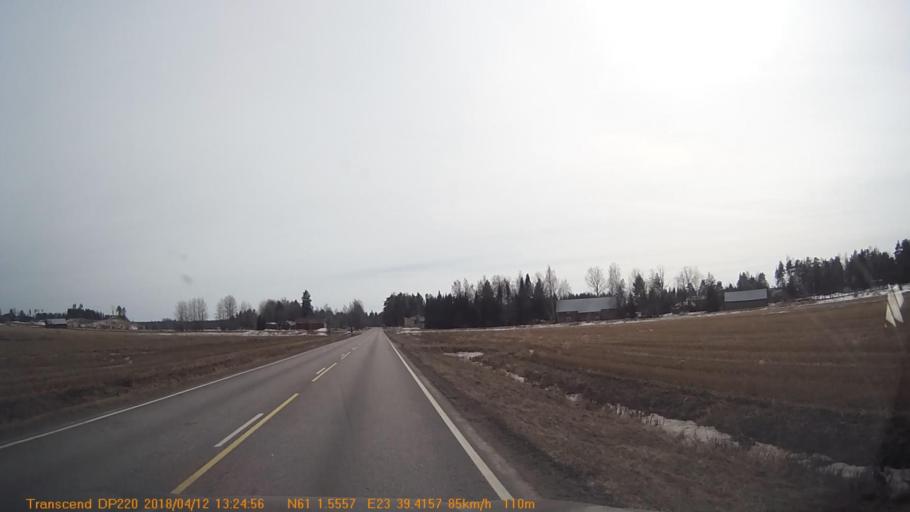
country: FI
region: Pirkanmaa
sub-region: Etelae-Pirkanmaa
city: Kylmaekoski
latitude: 61.0248
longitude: 23.6578
